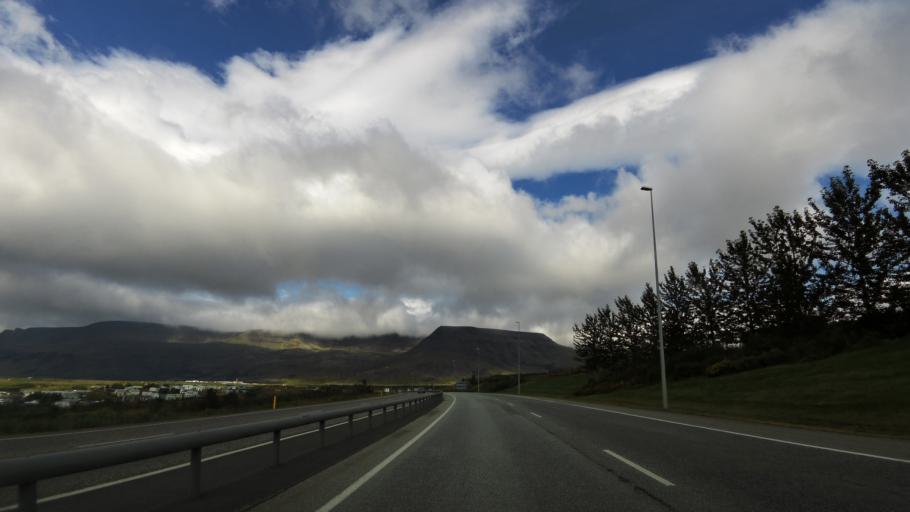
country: IS
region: Capital Region
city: Mosfellsbaer
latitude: 64.1727
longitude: -21.6769
